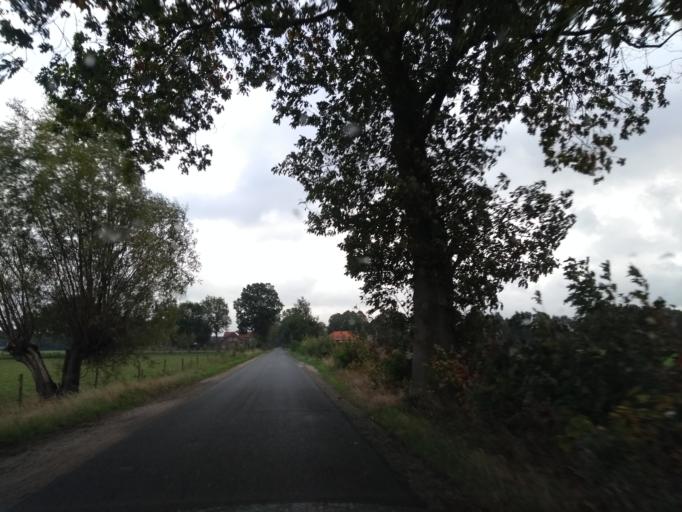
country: NL
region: Gelderland
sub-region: Gemeente Bronckhorst
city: Zelhem
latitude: 52.0140
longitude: 6.3826
